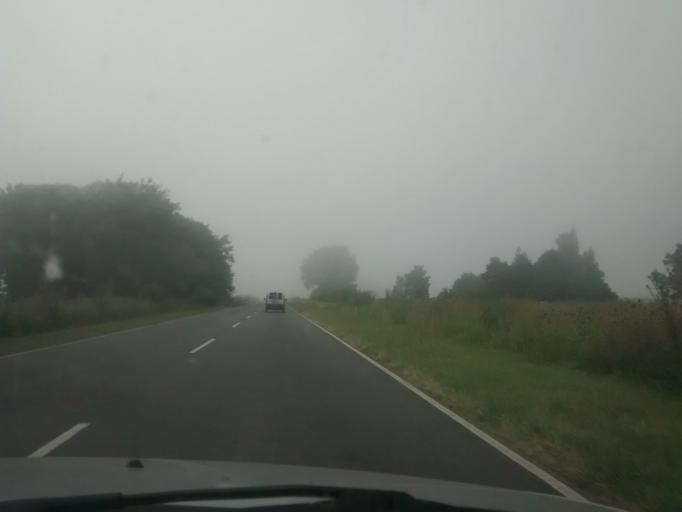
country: AR
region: Buenos Aires
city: Ranchos
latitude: -35.3586
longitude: -58.2494
